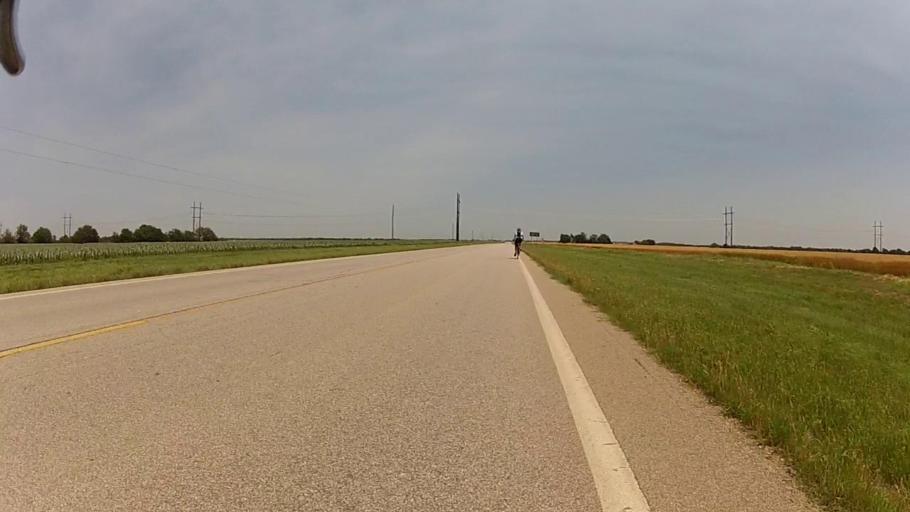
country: US
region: Kansas
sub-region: Cowley County
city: Arkansas City
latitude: 37.0561
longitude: -97.1383
